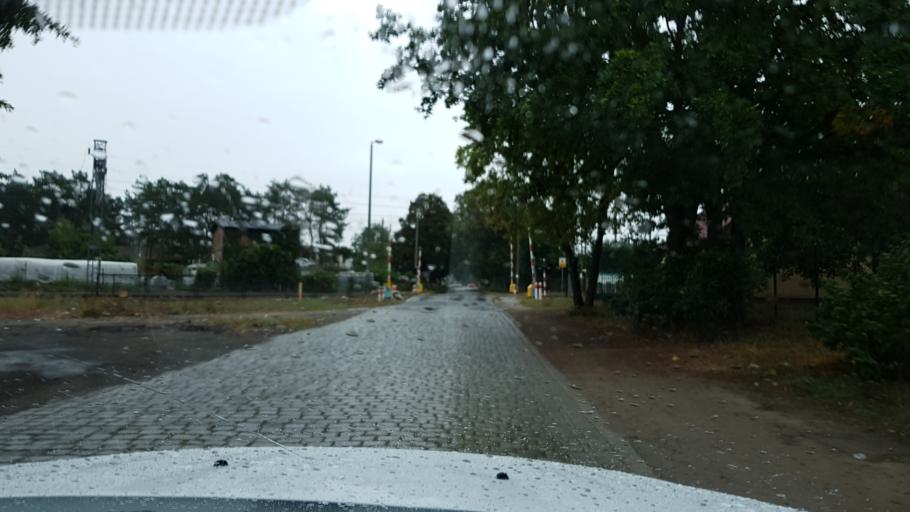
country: PL
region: West Pomeranian Voivodeship
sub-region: Powiat gryfinski
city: Gryfino
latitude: 53.2225
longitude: 14.4874
